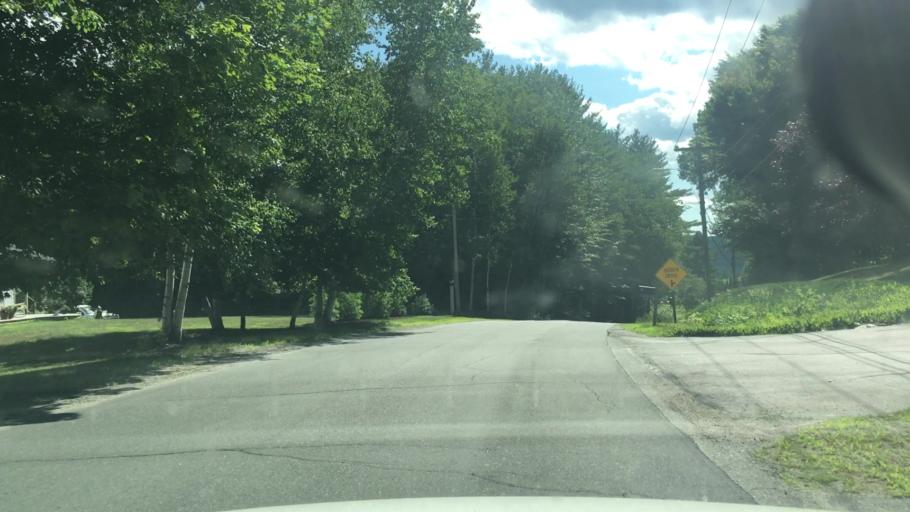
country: US
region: Maine
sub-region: Franklin County
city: Farmington
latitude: 44.6661
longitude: -70.1332
